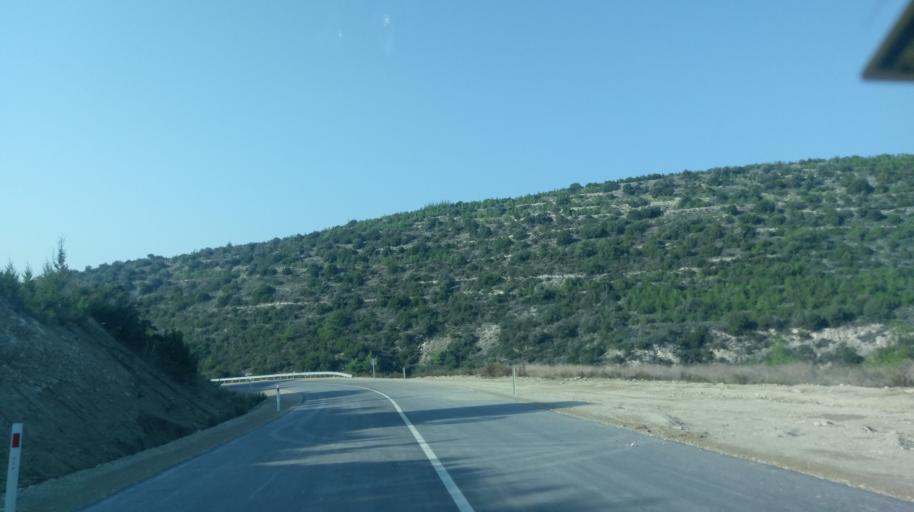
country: CY
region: Ammochostos
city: Leonarisso
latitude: 35.5344
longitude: 34.2519
